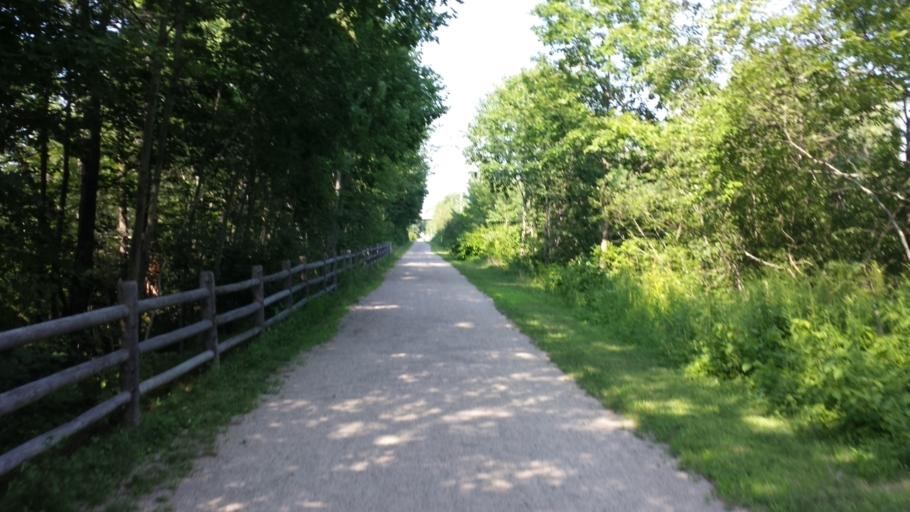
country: US
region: Maine
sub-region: York County
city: Biddeford
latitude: 43.4699
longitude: -70.4942
